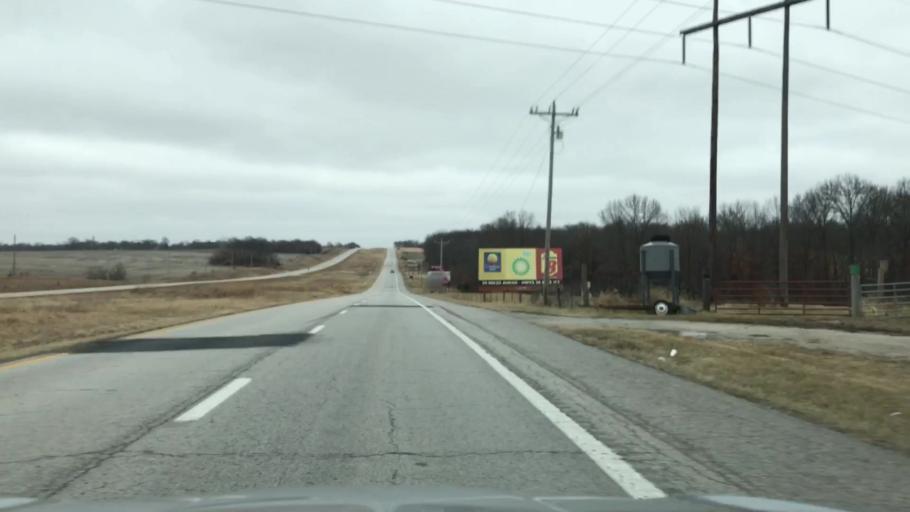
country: US
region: Missouri
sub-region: Linn County
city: Linneus
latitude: 39.7780
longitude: -93.1954
